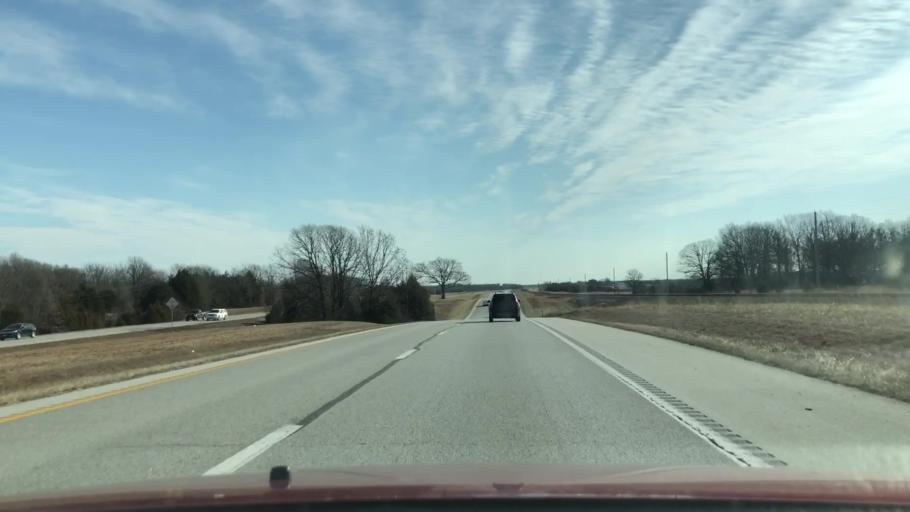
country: US
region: Missouri
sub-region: Webster County
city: Seymour
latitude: 37.1302
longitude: -92.7178
